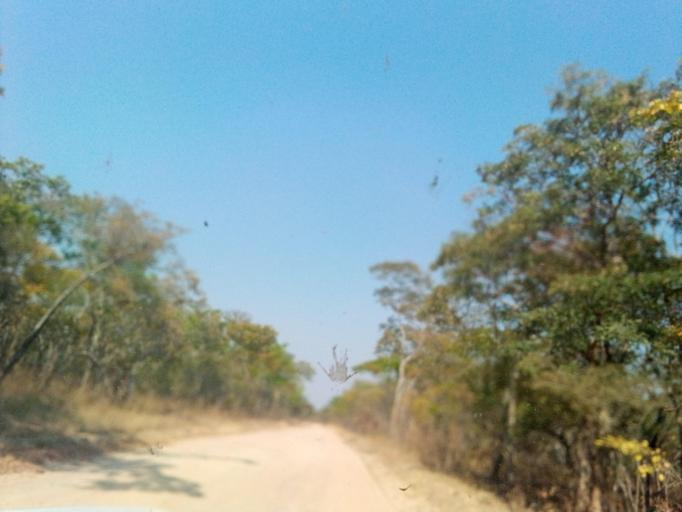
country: ZM
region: Northern
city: Mpika
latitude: -12.2267
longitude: 30.8914
